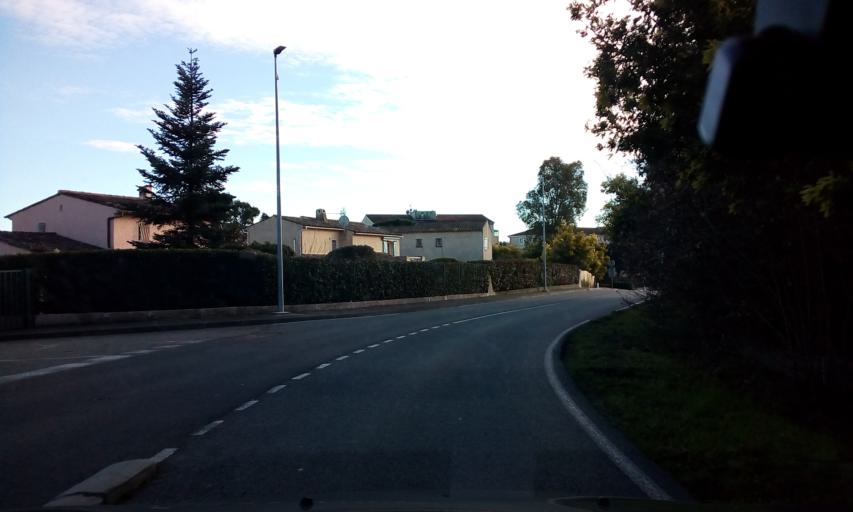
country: FR
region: Provence-Alpes-Cote d'Azur
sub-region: Departement du Var
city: Saint-Raphael
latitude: 43.4380
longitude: 6.7670
